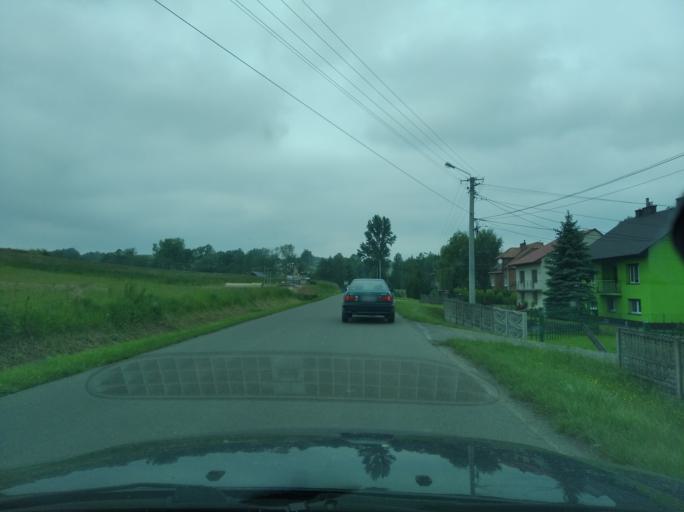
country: PL
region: Subcarpathian Voivodeship
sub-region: Powiat ropczycko-sedziszowski
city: Sedziszow Malopolski
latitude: 50.0444
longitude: 21.7002
